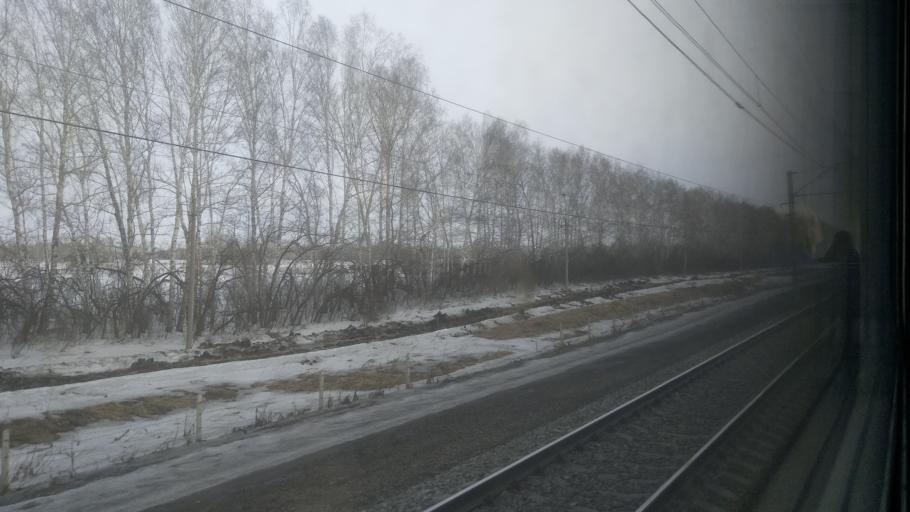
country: RU
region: Novosibirsk
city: Bolotnoye
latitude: 55.7032
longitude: 84.5832
